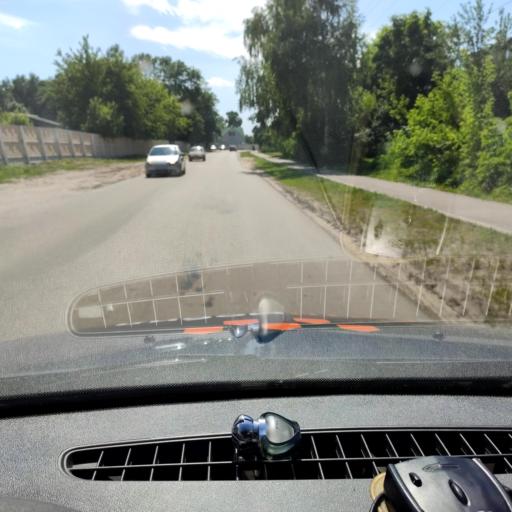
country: RU
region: Voronezj
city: Ramon'
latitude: 51.8262
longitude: 39.2643
